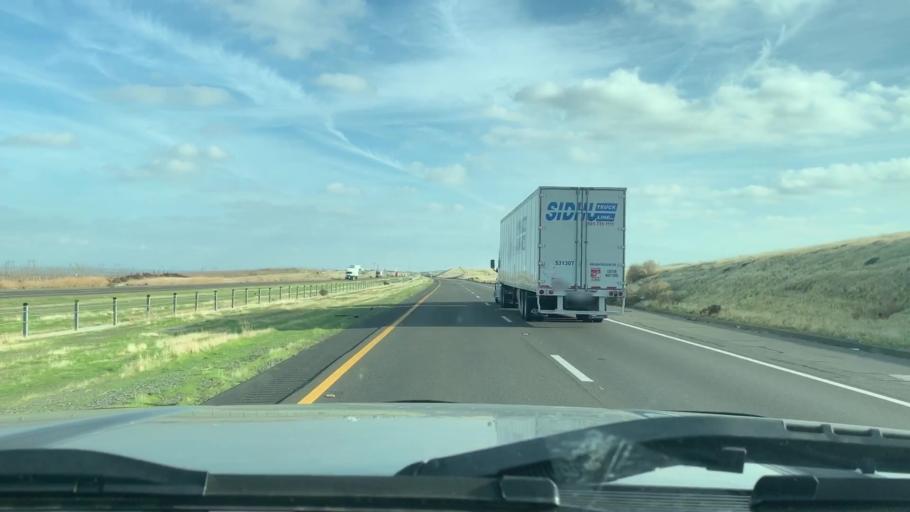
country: US
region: California
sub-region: Kings County
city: Avenal
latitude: 36.0478
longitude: -120.0543
